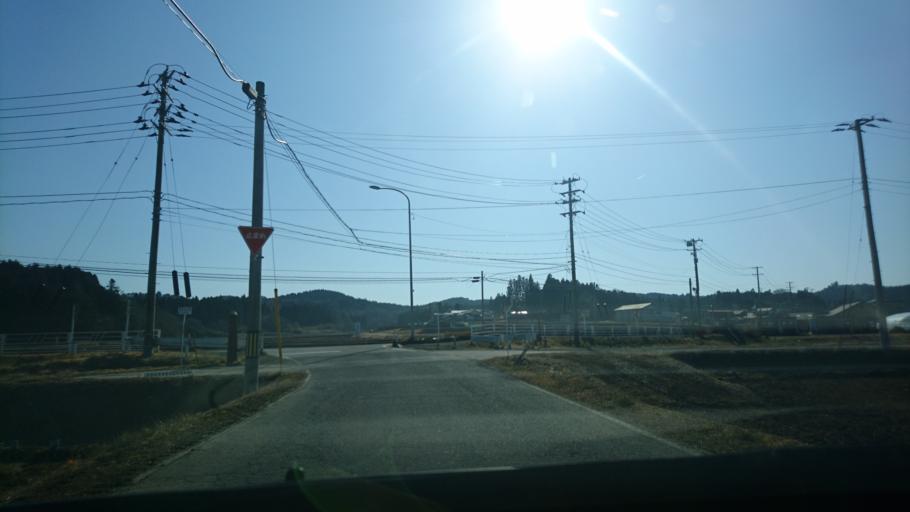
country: JP
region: Iwate
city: Ichinoseki
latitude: 38.8375
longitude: 141.2381
